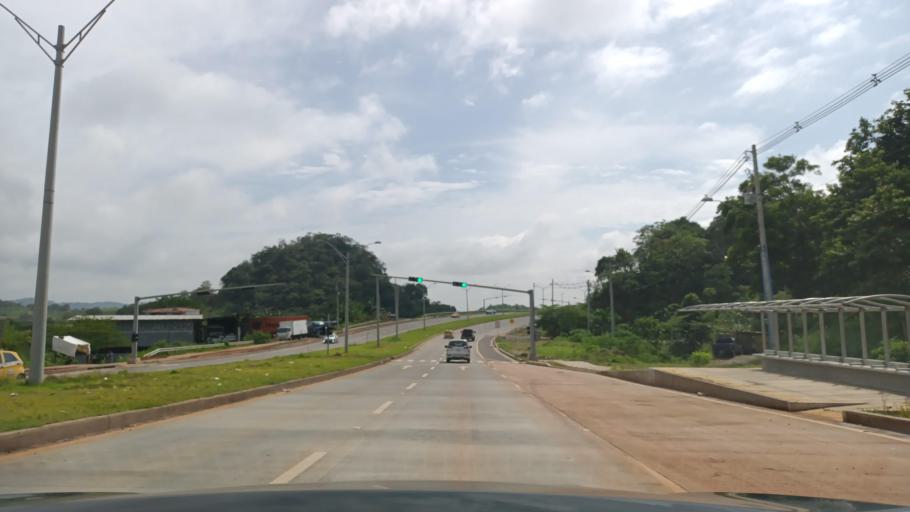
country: PA
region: Panama
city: Las Cumbres
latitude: 9.1003
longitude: -79.4906
